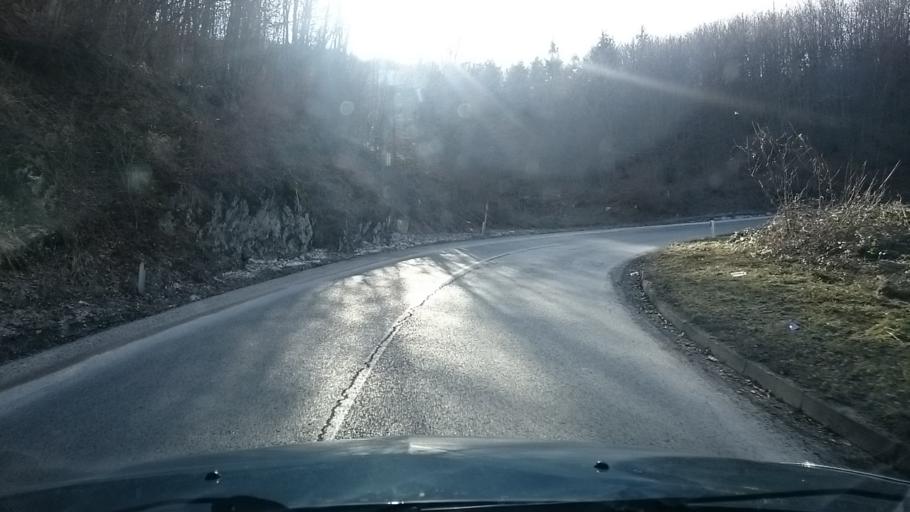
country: BA
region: Republika Srpska
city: Starcevica
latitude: 44.6823
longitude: 17.2125
